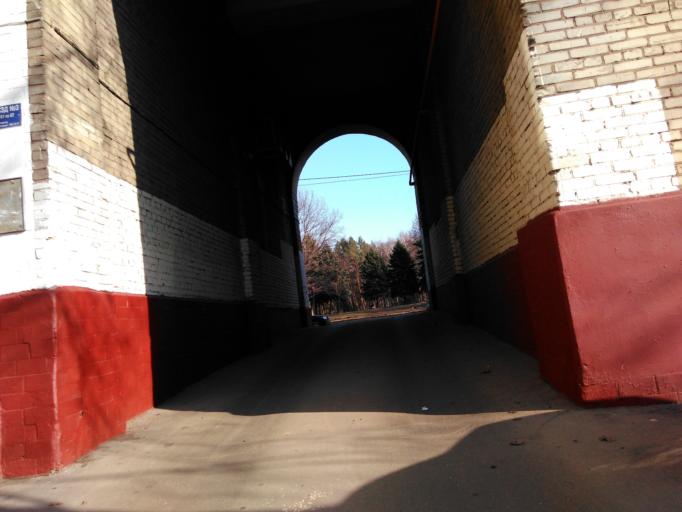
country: RU
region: Moscow
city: Vorob'yovo
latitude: 55.7129
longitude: 37.5224
